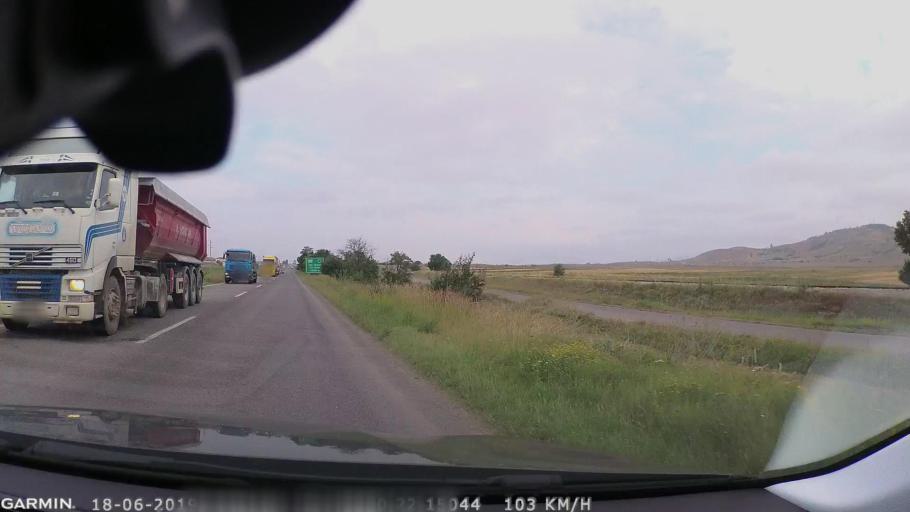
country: MK
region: Stip
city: Shtip
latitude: 41.7693
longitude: 22.1494
